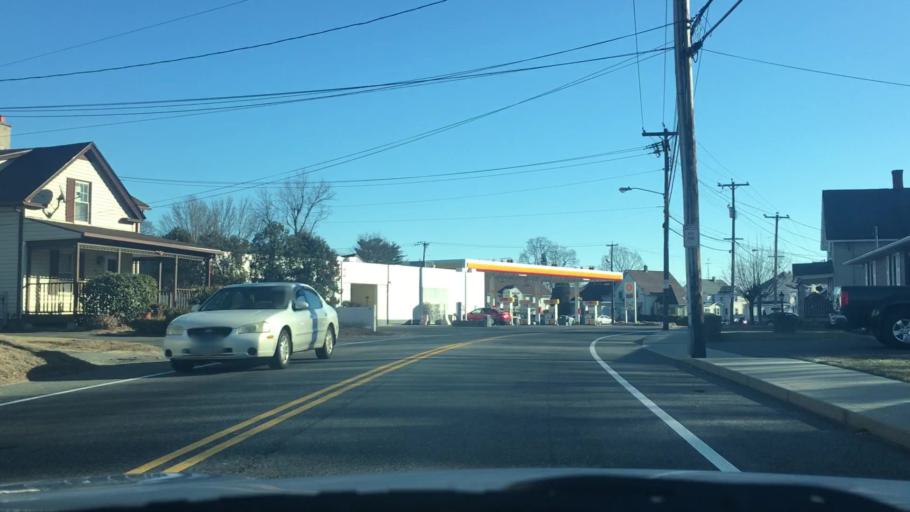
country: US
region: Massachusetts
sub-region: Hampden County
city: Ludlow
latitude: 42.1642
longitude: -72.4844
